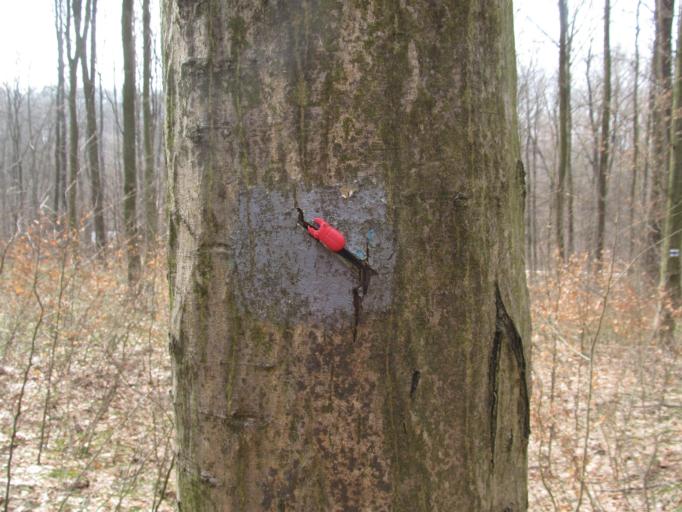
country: HU
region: Veszprem
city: Herend
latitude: 47.2177
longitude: 17.6544
